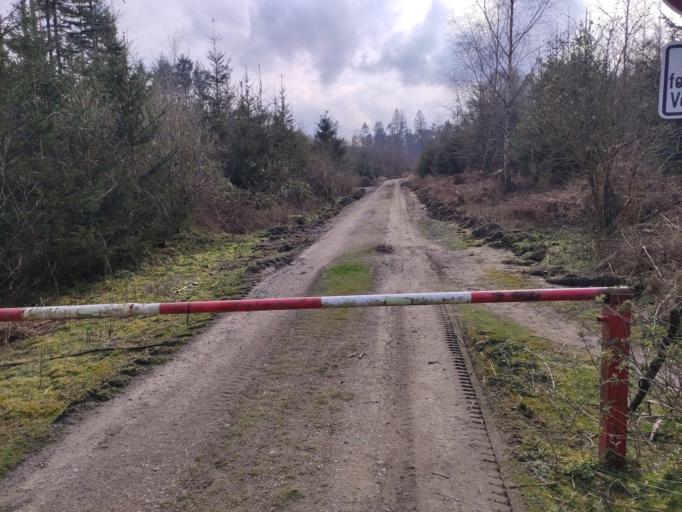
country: DE
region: North Rhine-Westphalia
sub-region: Regierungsbezirk Munster
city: Klein Reken
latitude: 51.7781
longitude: 7.0983
